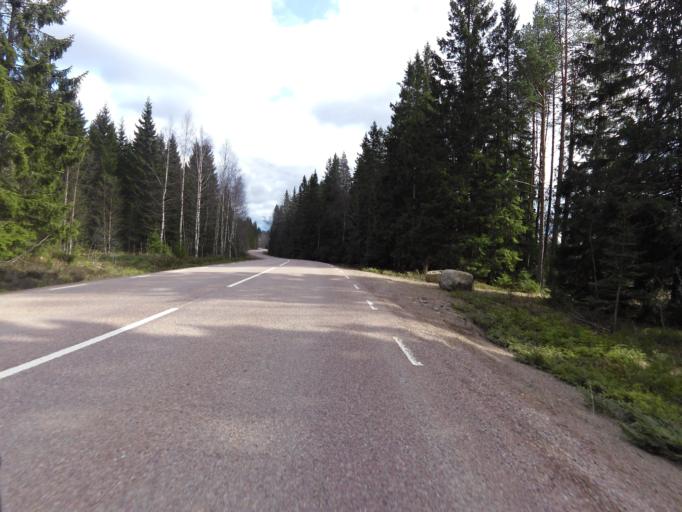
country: SE
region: Dalarna
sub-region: Avesta Kommun
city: Horndal
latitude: 60.2941
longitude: 16.2903
